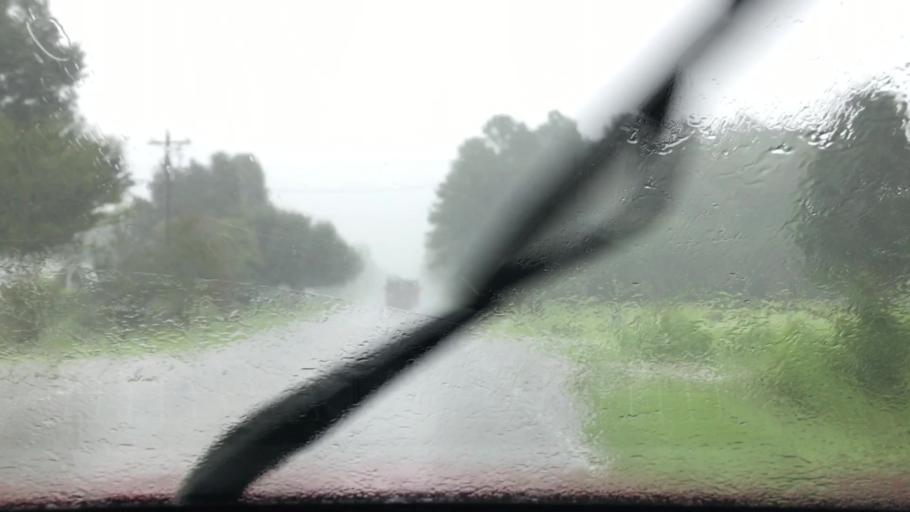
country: US
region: South Carolina
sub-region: Horry County
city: Red Hill
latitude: 33.9002
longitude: -78.9236
